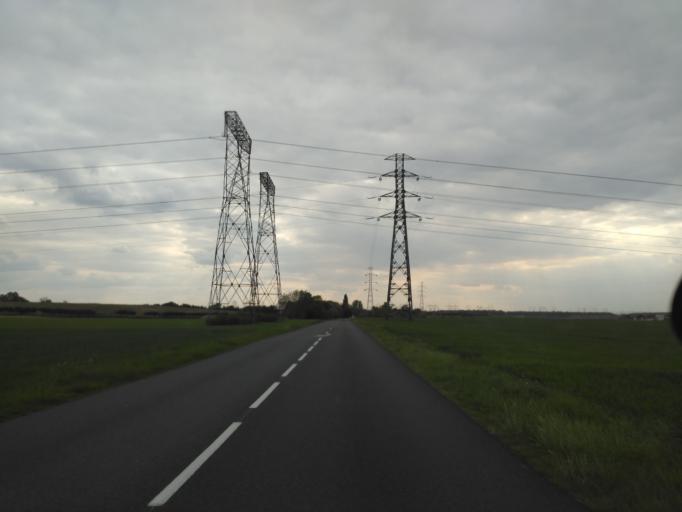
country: FR
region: Ile-de-France
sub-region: Departement de Seine-et-Marne
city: Moisenay
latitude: 48.5711
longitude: 2.7652
